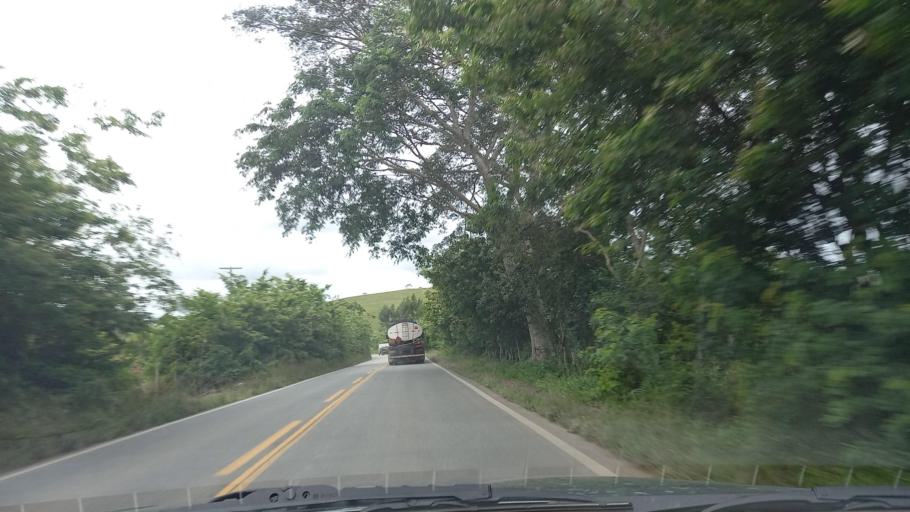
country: BR
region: Pernambuco
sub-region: Canhotinho
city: Canhotinho
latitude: -8.8707
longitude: -36.1954
